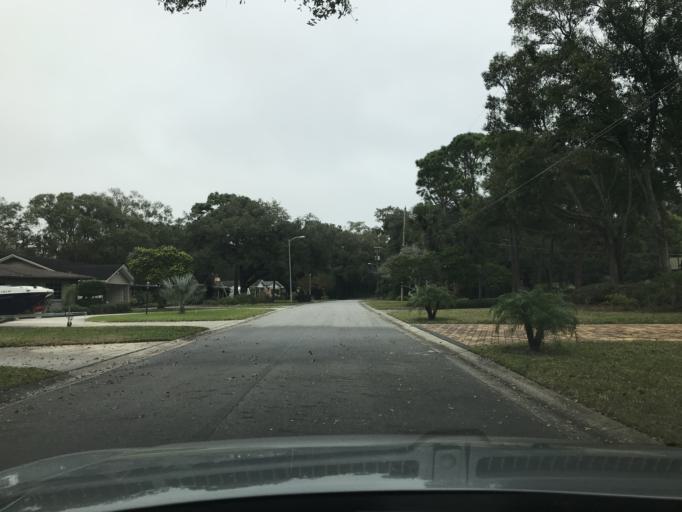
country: US
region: Florida
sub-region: Hillsborough County
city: Tampa
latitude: 27.9892
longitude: -82.4704
